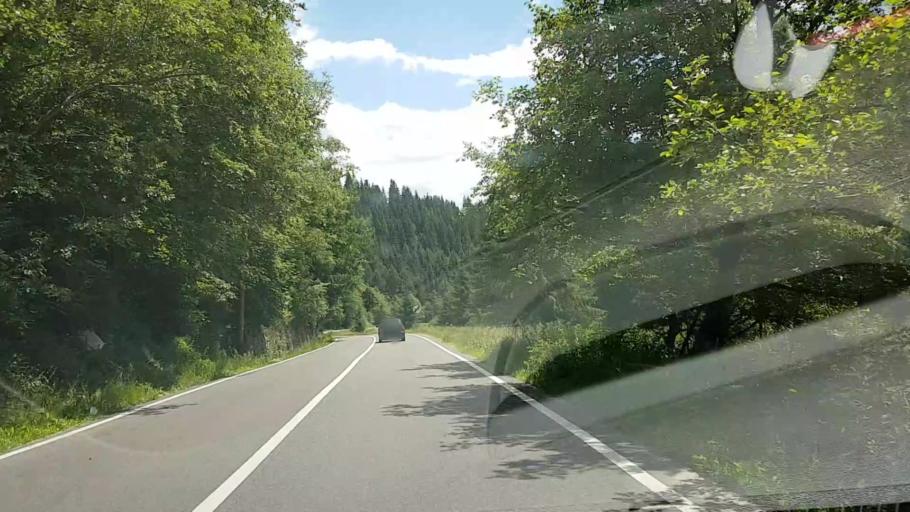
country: RO
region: Suceava
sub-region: Comuna Brosteni
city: Brosteni
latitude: 47.2634
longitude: 25.6652
